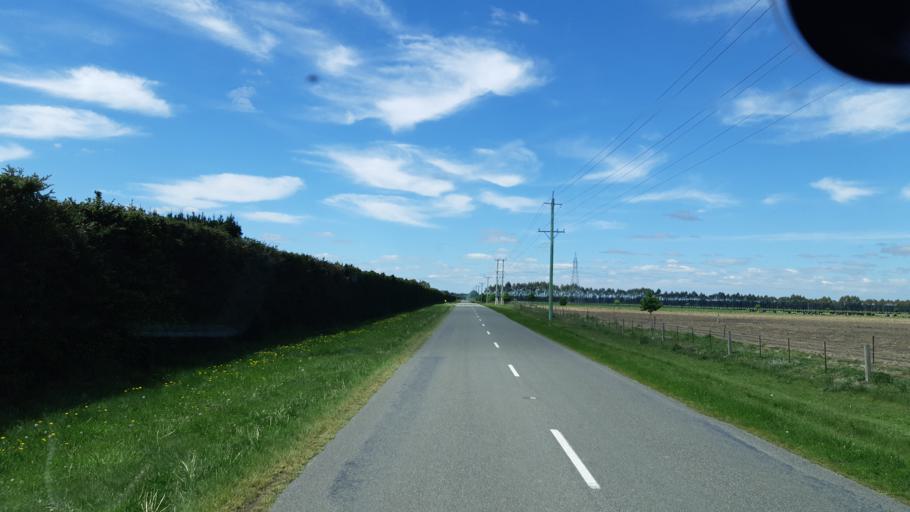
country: NZ
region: Canterbury
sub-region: Ashburton District
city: Methven
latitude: -43.7233
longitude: 171.4811
